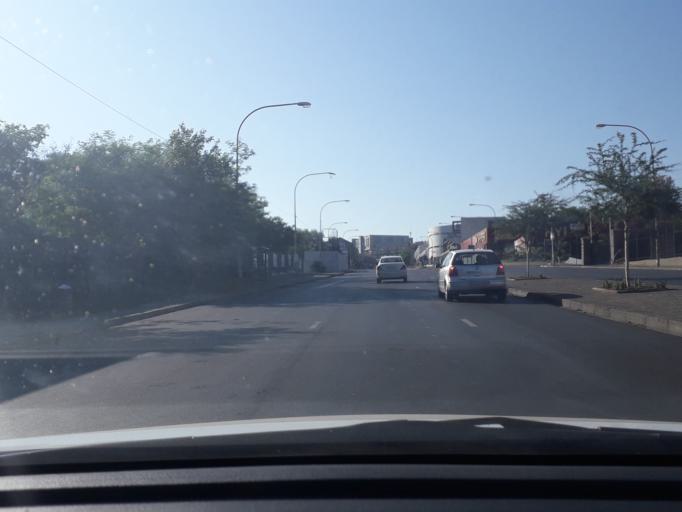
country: ZA
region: Gauteng
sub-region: City of Johannesburg Metropolitan Municipality
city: Johannesburg
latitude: -26.1180
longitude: 28.0257
